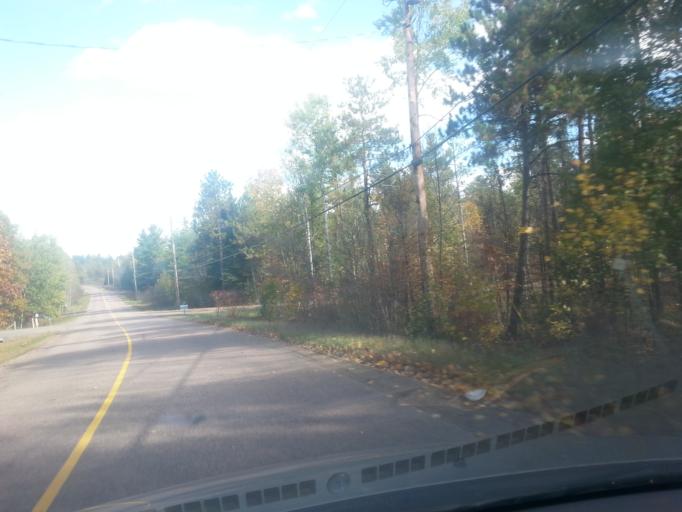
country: CA
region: Ontario
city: Renfrew
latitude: 45.5023
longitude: -76.9633
